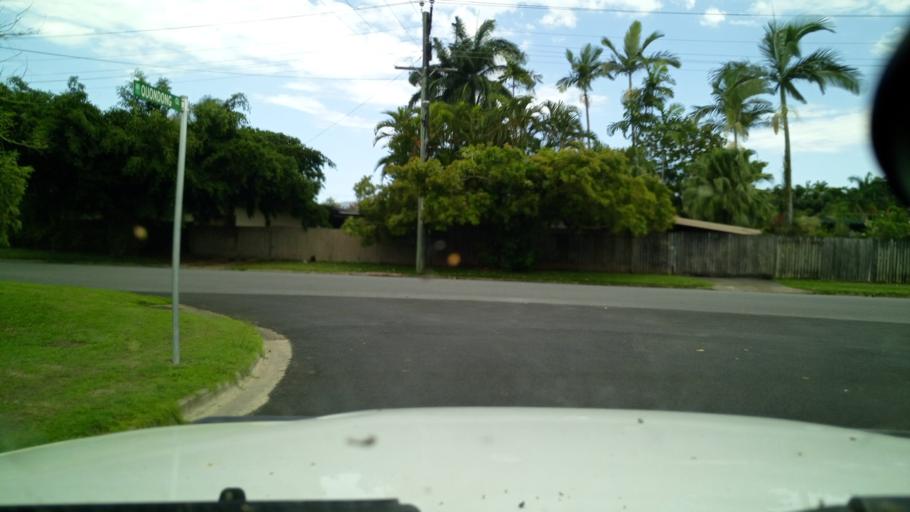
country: AU
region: Queensland
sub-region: Cairns
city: Cairns
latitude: -16.9162
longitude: 145.7362
